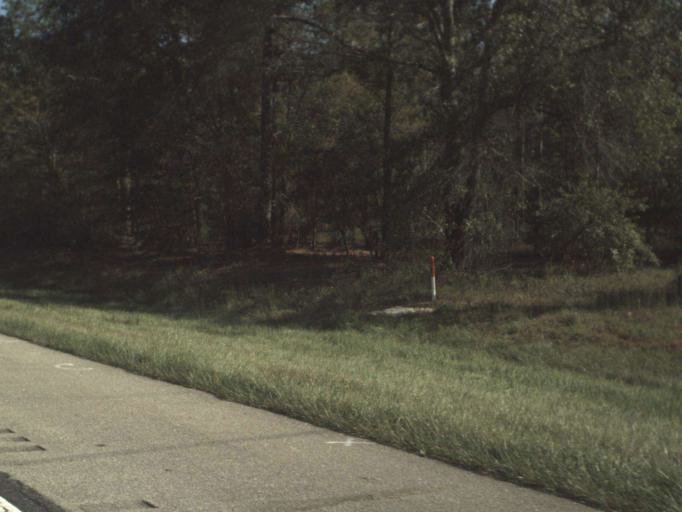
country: US
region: Florida
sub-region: Washington County
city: Chipley
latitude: 30.7460
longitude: -85.4996
